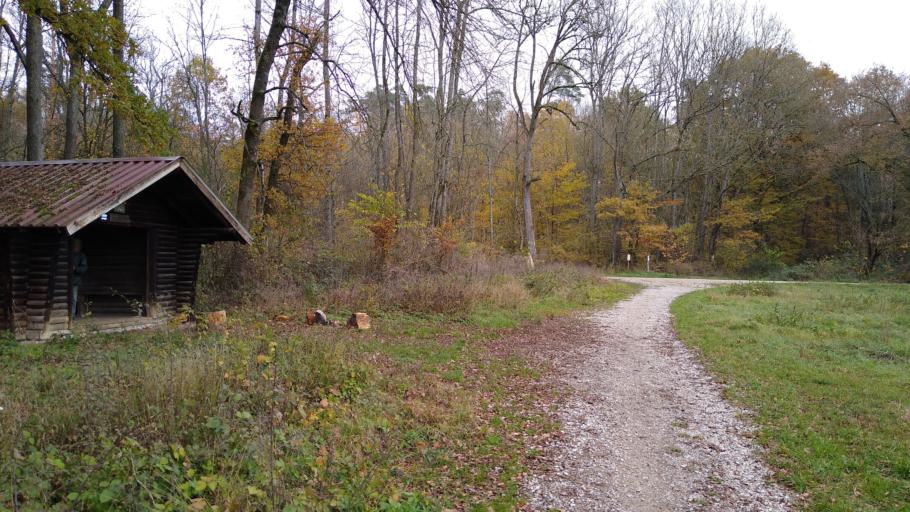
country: DE
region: Bavaria
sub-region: Regierungsbezirk Mittelfranken
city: Kalchreuth
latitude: 49.5455
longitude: 11.1042
